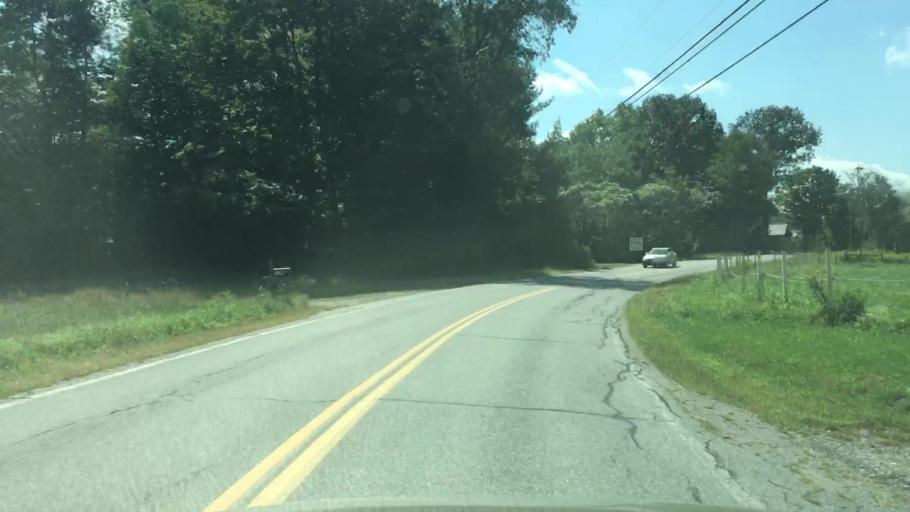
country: US
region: Vermont
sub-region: Windham County
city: West Brattleboro
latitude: 42.7853
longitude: -72.6001
